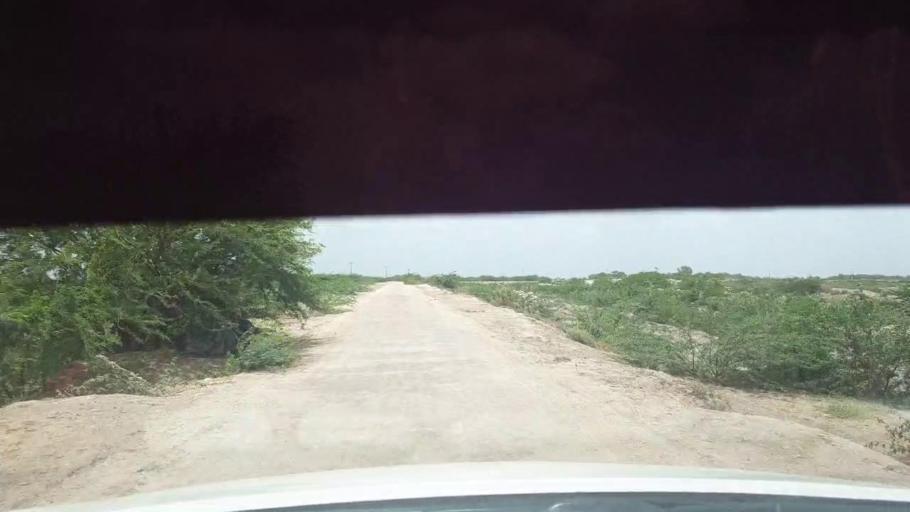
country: PK
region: Sindh
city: Kadhan
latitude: 24.4851
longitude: 69.0669
